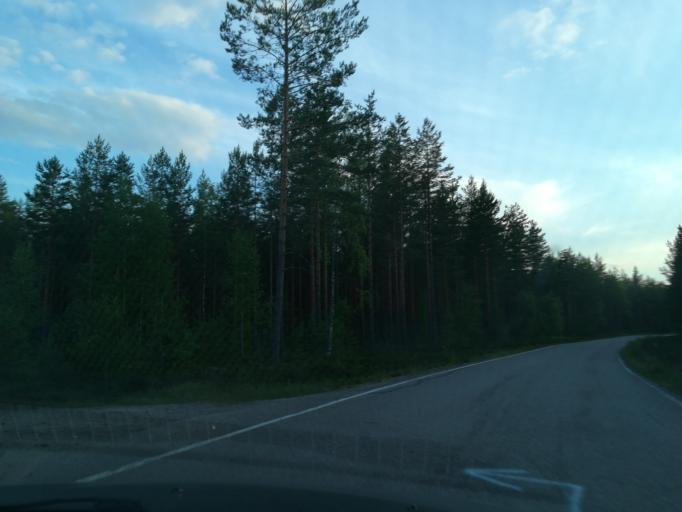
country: FI
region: South Karelia
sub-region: Lappeenranta
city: Joutseno
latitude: 61.3433
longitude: 28.4028
